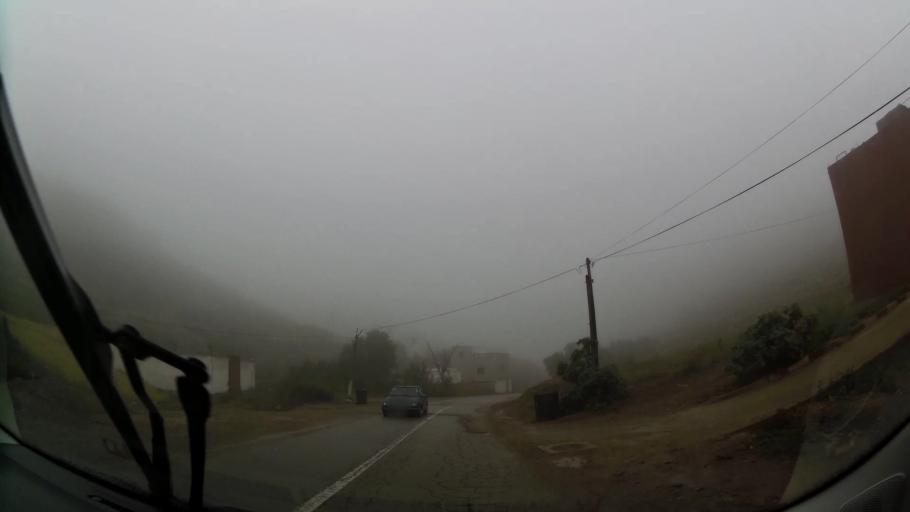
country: MA
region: Taza-Al Hoceima-Taounate
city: Tirhanimine
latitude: 35.2303
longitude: -3.9685
